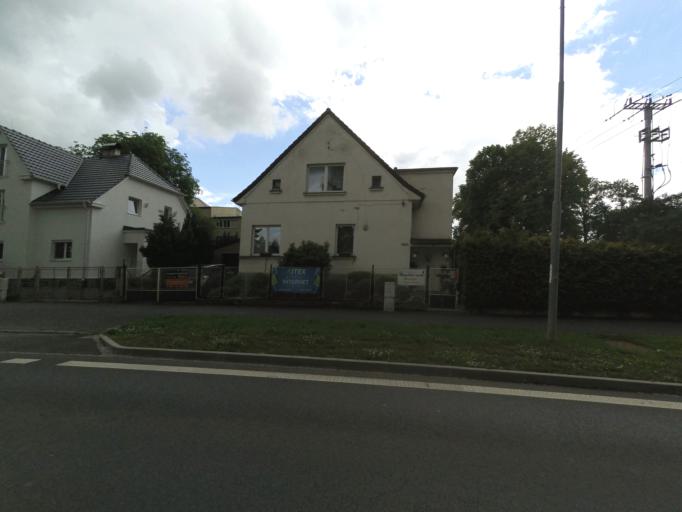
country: CZ
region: Plzensky
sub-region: Okres Domazlice
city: Domazlice
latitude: 49.4350
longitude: 12.9475
